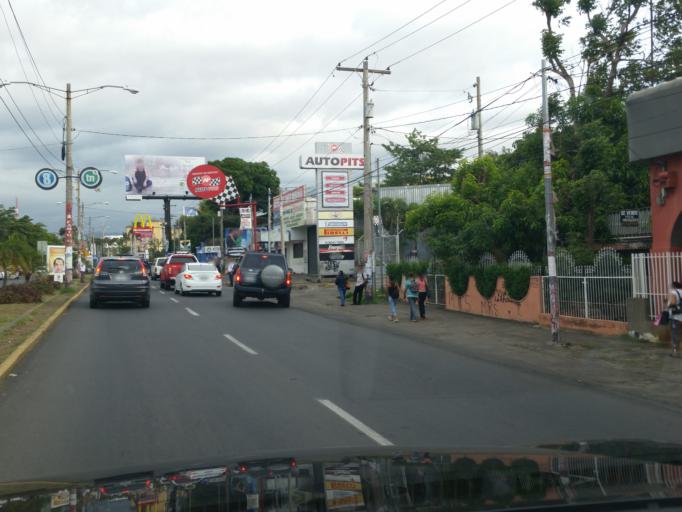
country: NI
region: Managua
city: Managua
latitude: 12.1278
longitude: -86.2660
